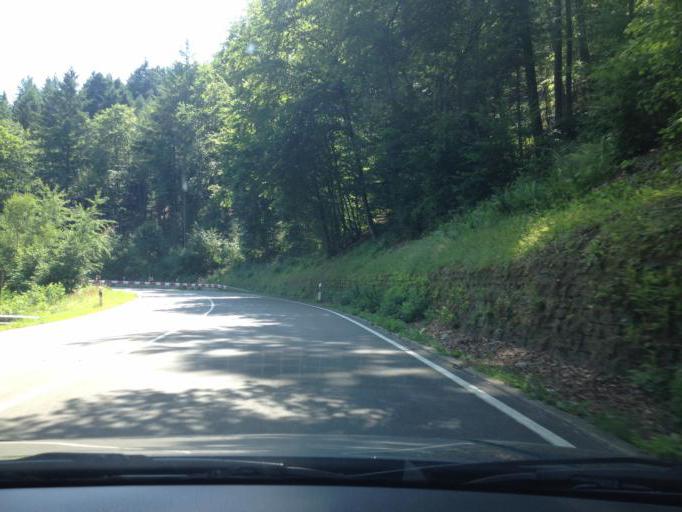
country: DE
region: Rheinland-Pfalz
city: Frankenstein
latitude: 49.4449
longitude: 7.9976
